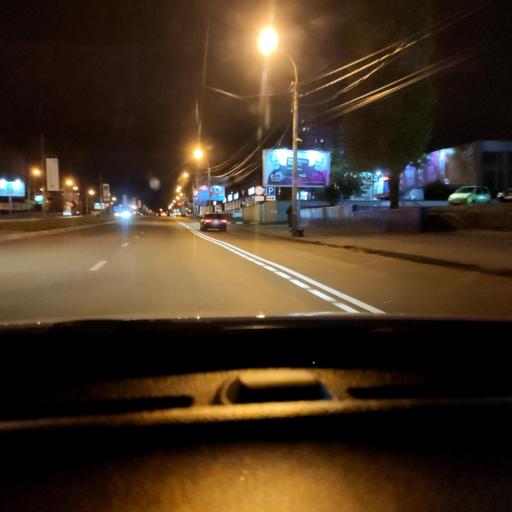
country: RU
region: Voronezj
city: Voronezh
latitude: 51.6879
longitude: 39.2551
